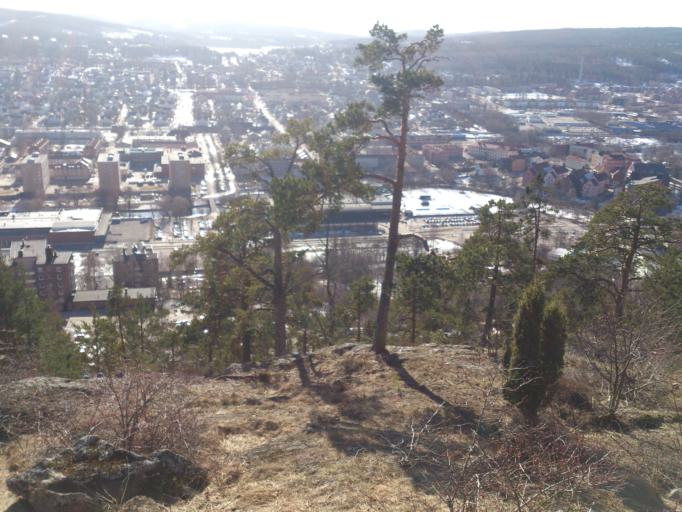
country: SE
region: Vaesternorrland
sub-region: Sundsvalls Kommun
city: Sundsvall
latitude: 62.3984
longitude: 17.2943
